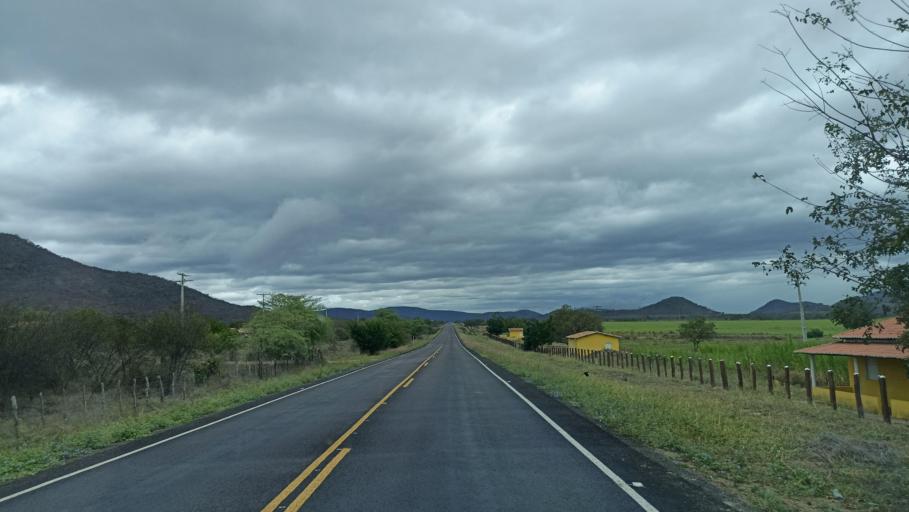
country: BR
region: Bahia
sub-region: Iacu
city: Iacu
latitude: -12.8918
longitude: -40.3970
